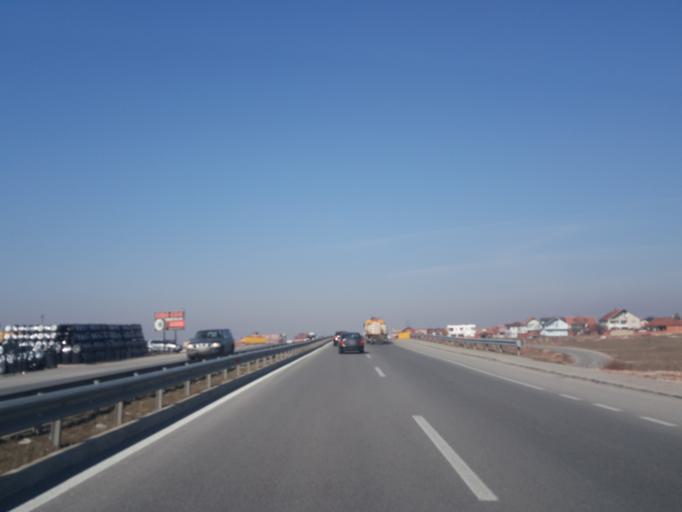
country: XK
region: Pristina
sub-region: Komuna e Obiliqit
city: Obiliq
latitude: 42.7596
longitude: 21.0316
